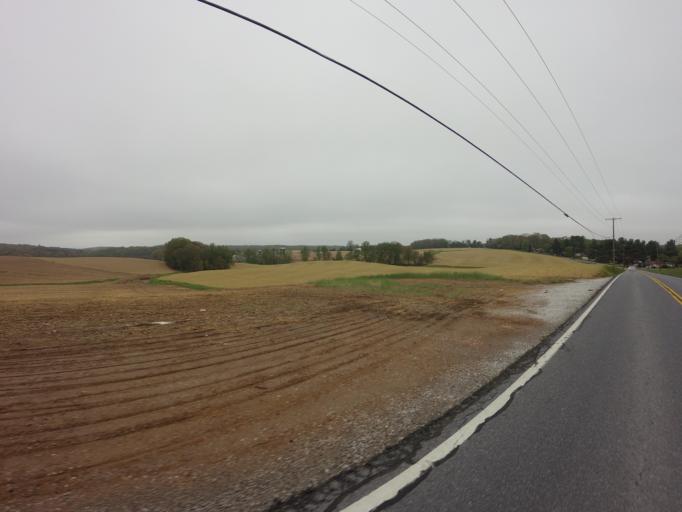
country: US
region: Maryland
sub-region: Baltimore County
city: Hunt Valley
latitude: 39.5932
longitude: -76.6823
